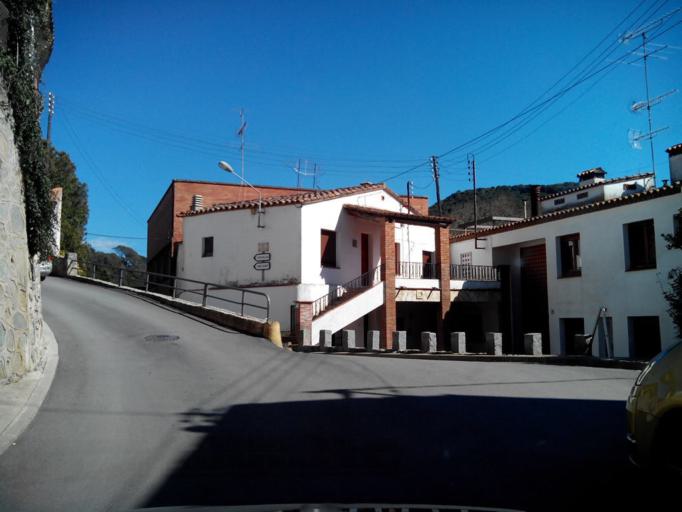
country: ES
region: Catalonia
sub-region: Provincia de Barcelona
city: Dosrius
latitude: 41.6009
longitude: 2.4474
